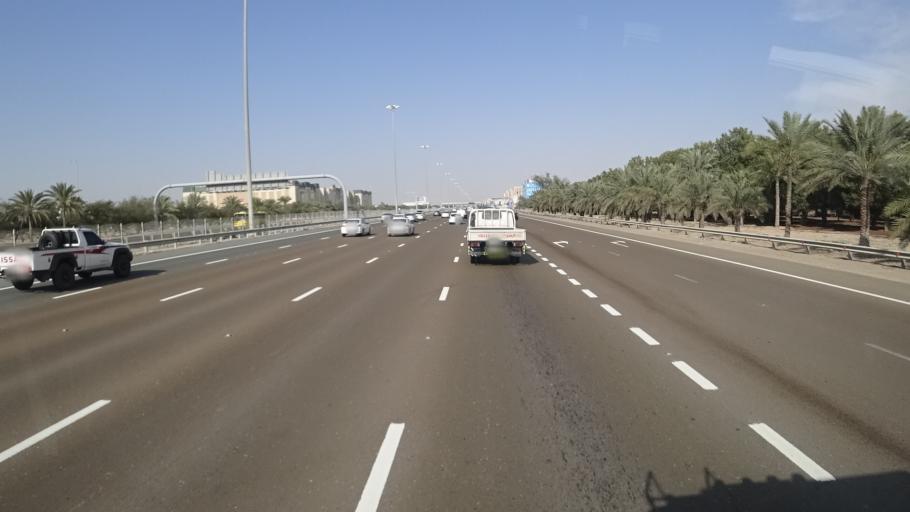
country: AE
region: Abu Dhabi
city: Abu Dhabi
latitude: 24.5169
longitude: 54.6689
